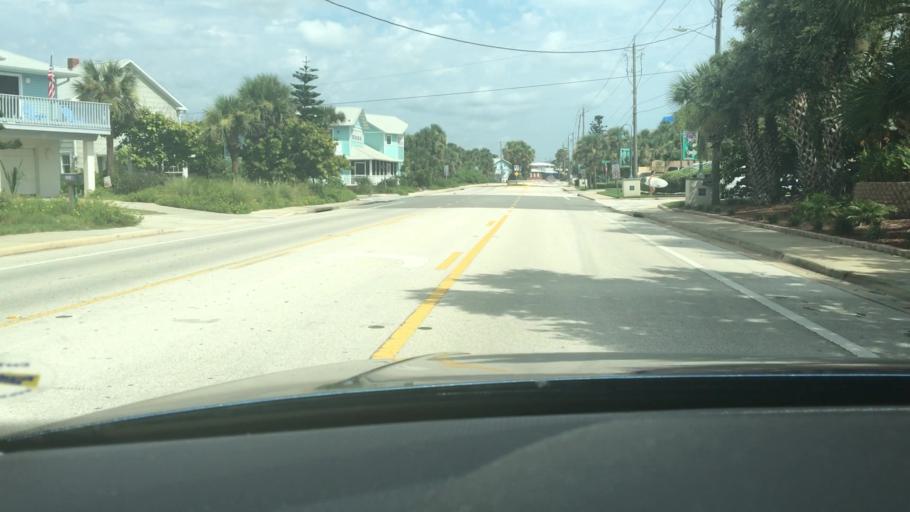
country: US
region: Florida
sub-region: Volusia County
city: New Smyrna Beach
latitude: 29.0357
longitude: -80.8951
